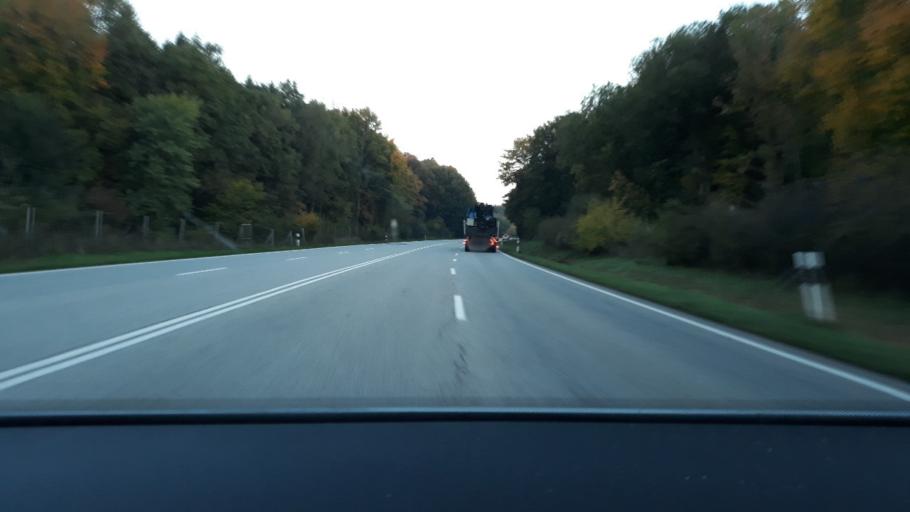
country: DE
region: Schleswig-Holstein
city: Schuby
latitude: 54.5177
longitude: 9.5126
